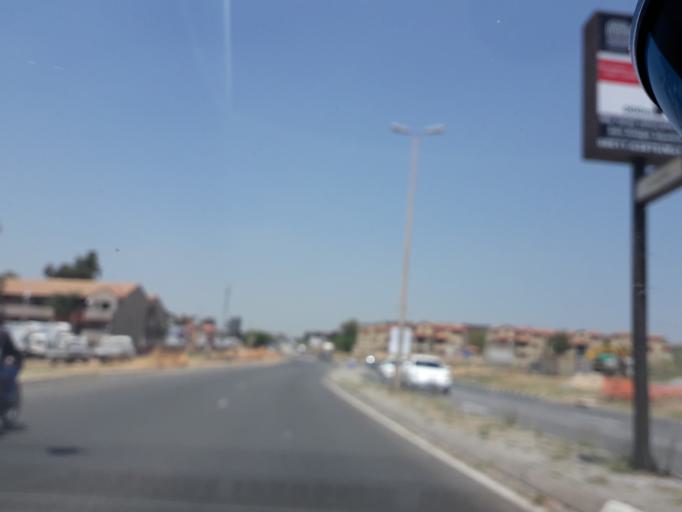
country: ZA
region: Gauteng
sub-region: City of Johannesburg Metropolitan Municipality
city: Midrand
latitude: -25.9688
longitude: 28.1207
